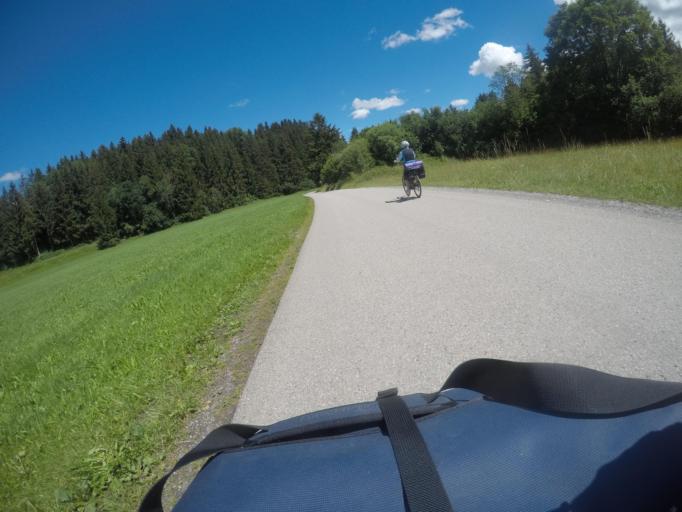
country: DE
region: Bavaria
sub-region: Upper Bavaria
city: Prem
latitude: 47.6828
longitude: 10.7922
